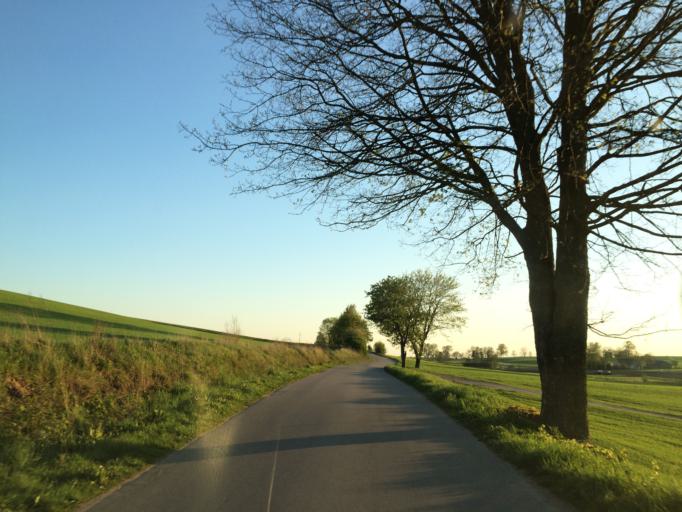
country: PL
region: Warmian-Masurian Voivodeship
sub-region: Powiat ilawski
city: Lubawa
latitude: 53.5019
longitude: 19.8450
